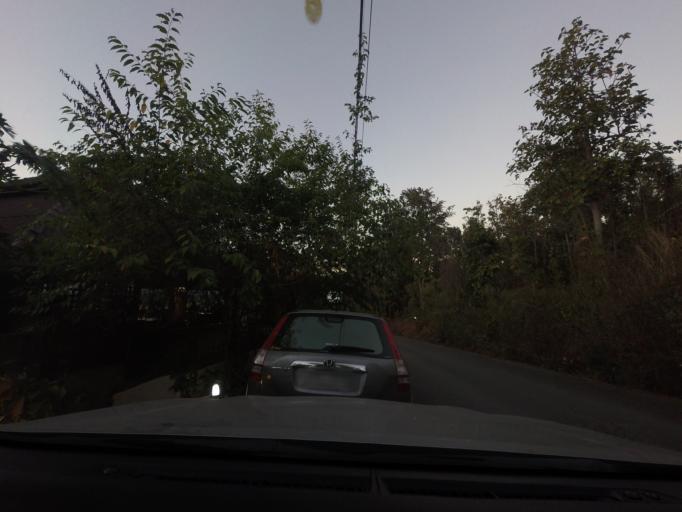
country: TH
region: Mae Hong Son
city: Mae Hi
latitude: 19.3496
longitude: 98.4524
